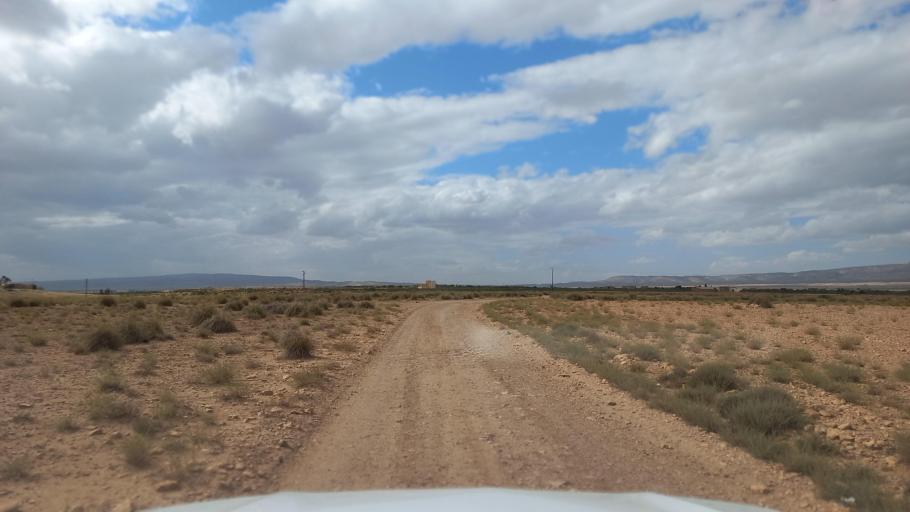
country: TN
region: Al Qasrayn
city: Sbiba
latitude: 35.3806
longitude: 9.1015
